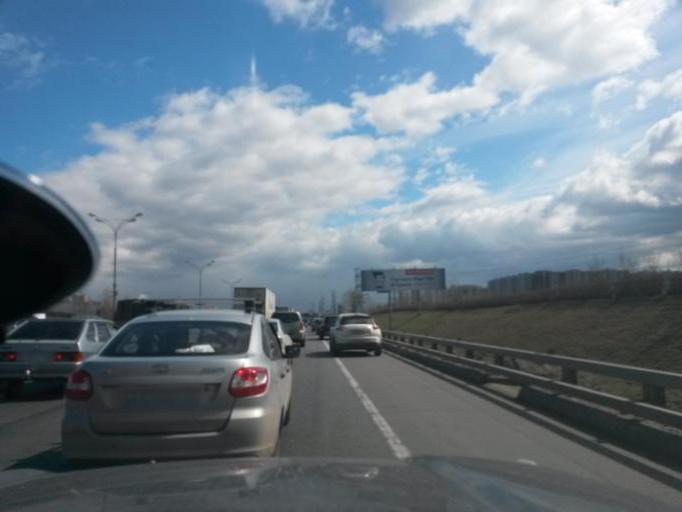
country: RU
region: Moscow
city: Chertanovo Yuzhnoye
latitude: 55.5822
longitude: 37.5672
